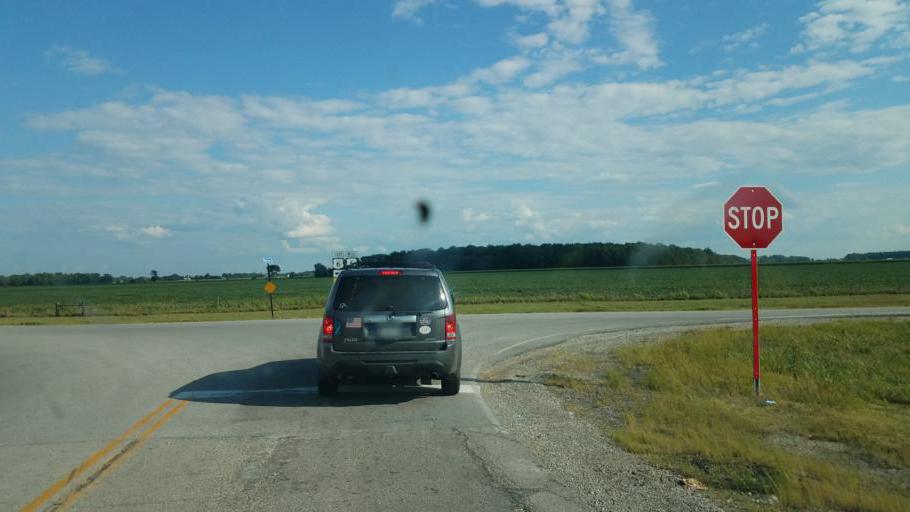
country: US
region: Ohio
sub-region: Wood County
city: Bowling Green
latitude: 41.3620
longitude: -83.5666
